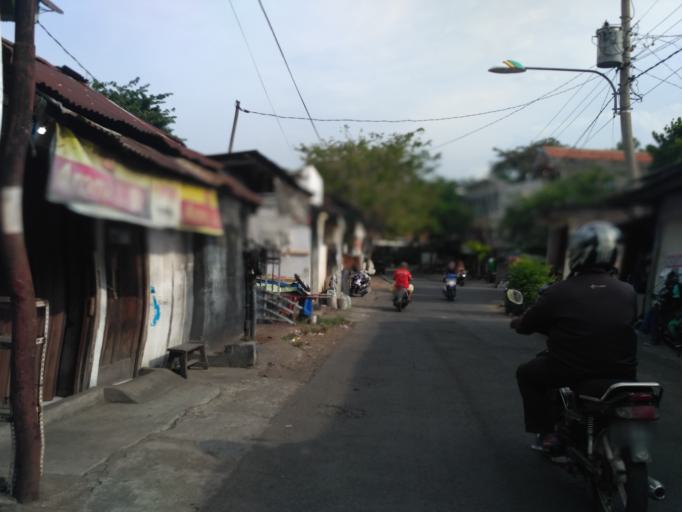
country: ID
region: Central Java
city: Semarang
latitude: -7.0114
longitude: 110.4410
